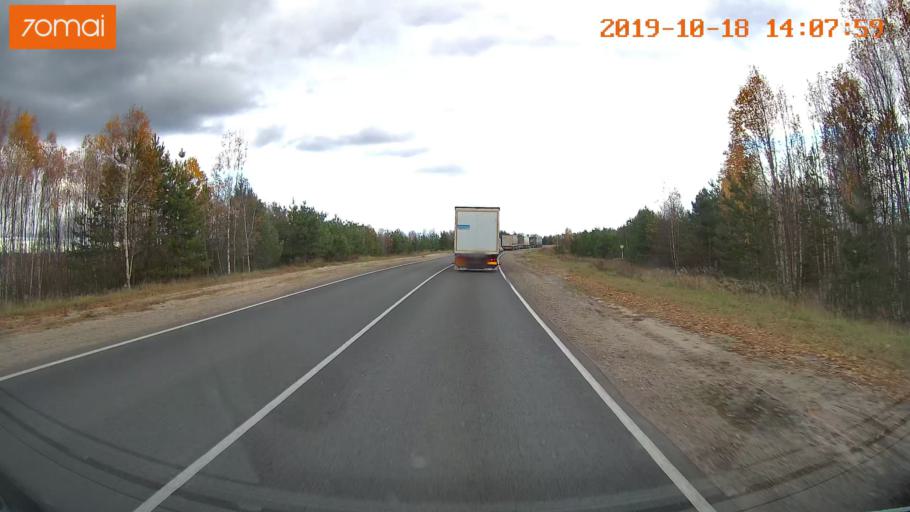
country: RU
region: Rjazan
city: Spas-Klepiki
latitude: 55.1516
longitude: 40.1669
